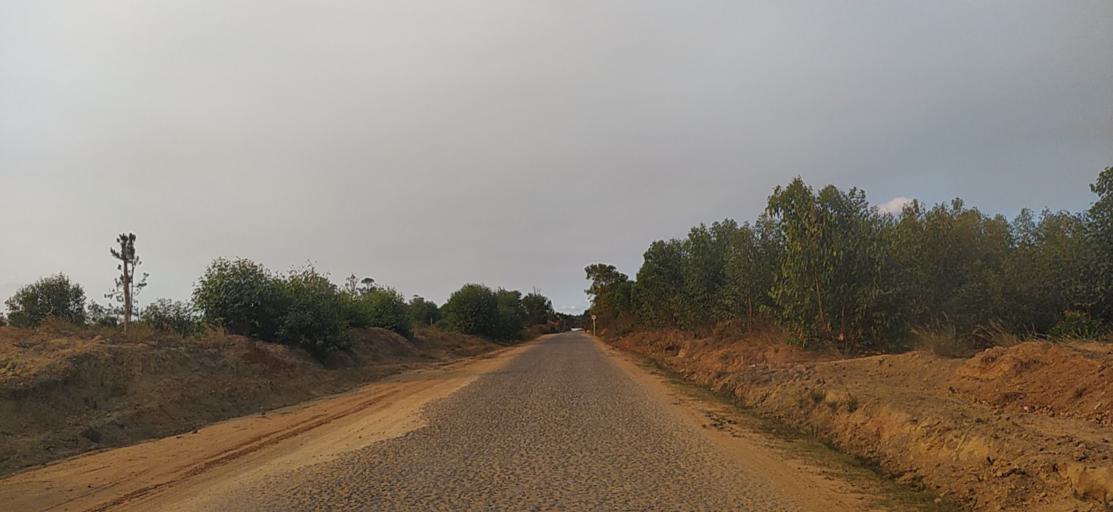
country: MG
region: Alaotra Mangoro
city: Moramanga
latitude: -18.6164
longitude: 48.2771
